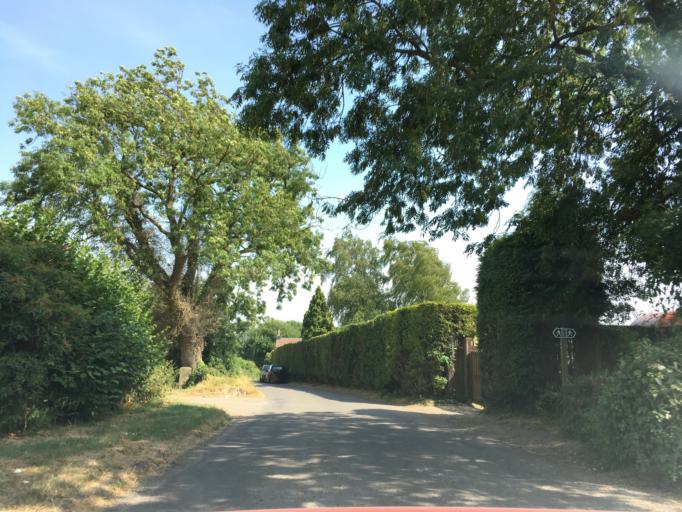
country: GB
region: England
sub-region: South Gloucestershire
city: Alveston
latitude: 51.5828
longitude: -2.5091
